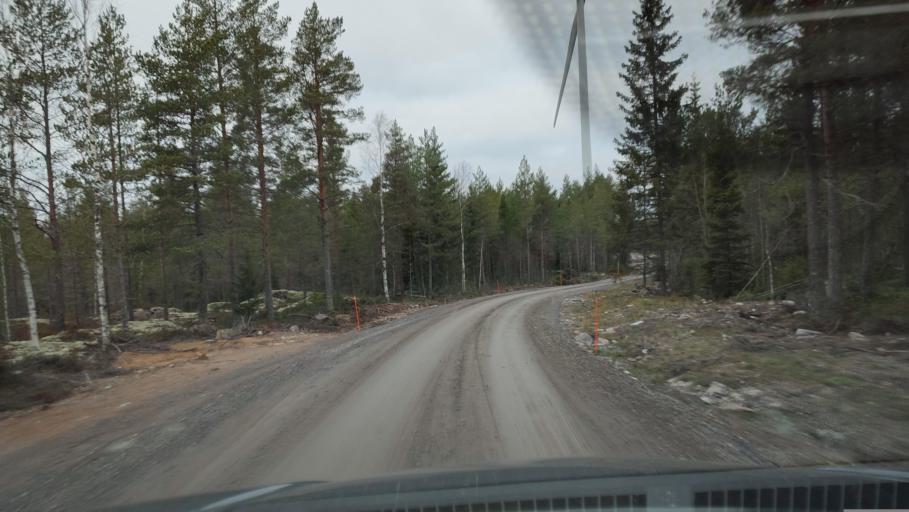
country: FI
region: Southern Ostrobothnia
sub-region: Suupohja
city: Karijoki
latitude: 62.2009
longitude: 21.5885
